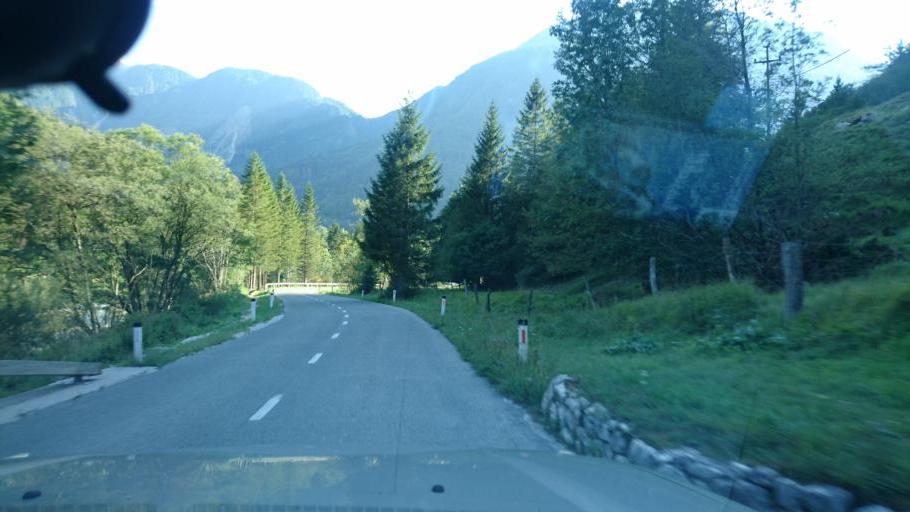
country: SI
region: Bovec
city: Bovec
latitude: 46.3435
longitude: 13.6851
